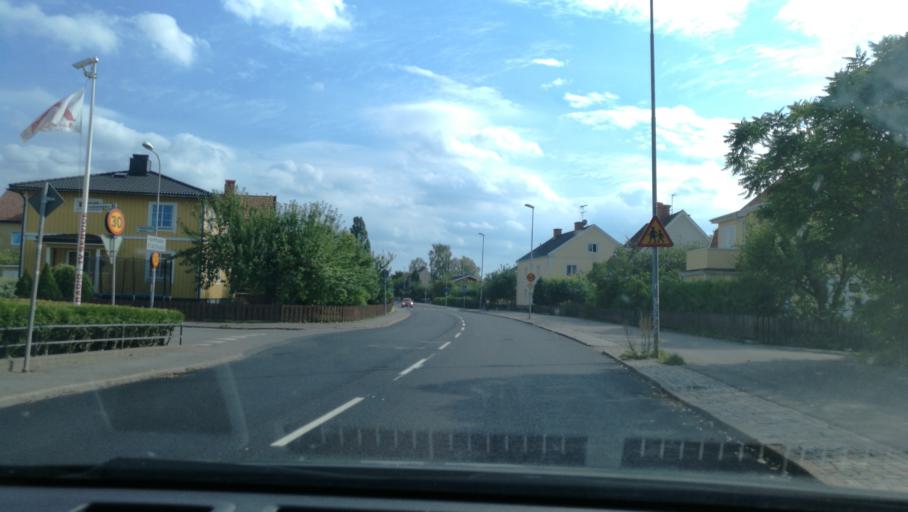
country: SE
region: Vaestmanland
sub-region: Vasteras
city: Vasteras
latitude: 59.6030
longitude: 16.5160
